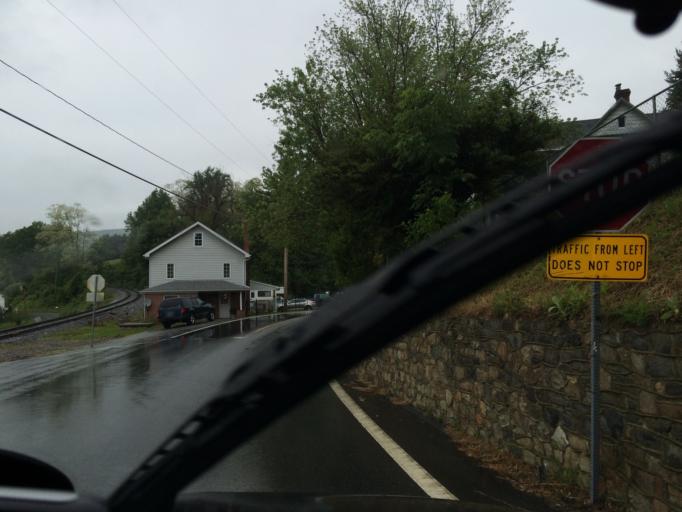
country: US
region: Maryland
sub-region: Washington County
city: Highfield-Cascade
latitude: 39.6739
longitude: -77.4546
